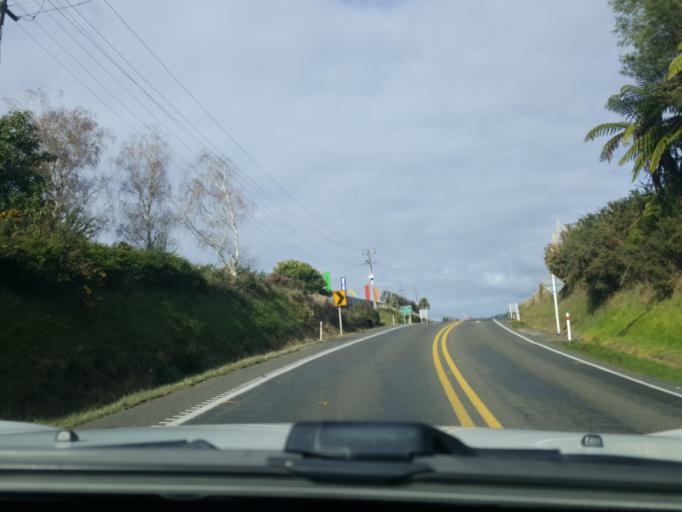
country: NZ
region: Bay of Plenty
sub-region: Tauranga City
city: Tauranga
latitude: -37.6847
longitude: 176.0366
